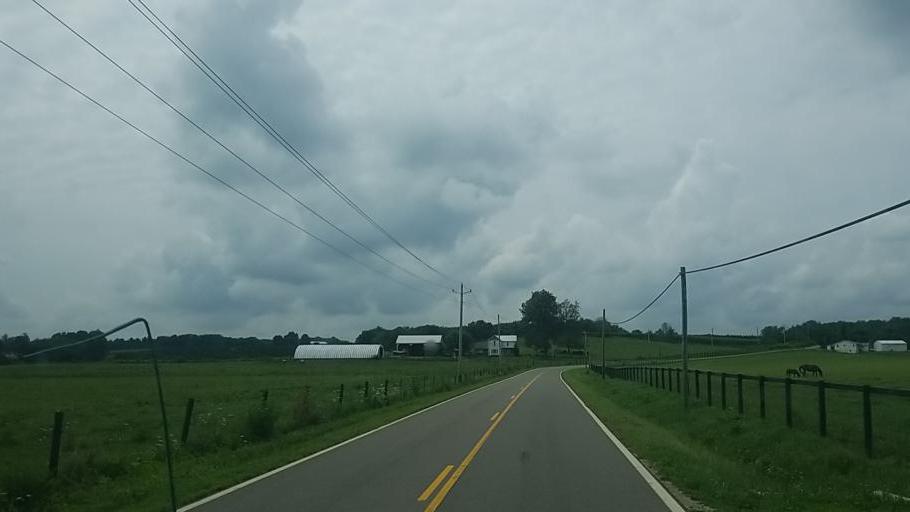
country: US
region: Ohio
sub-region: Licking County
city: Utica
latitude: 40.2021
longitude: -82.3632
